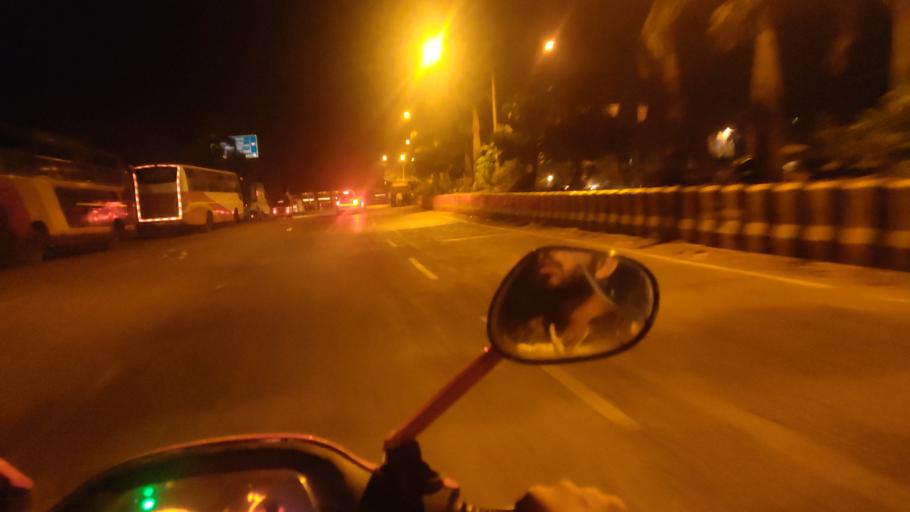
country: IN
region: Maharashtra
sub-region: Thane
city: Bhayandar
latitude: 19.2978
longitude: 72.8410
